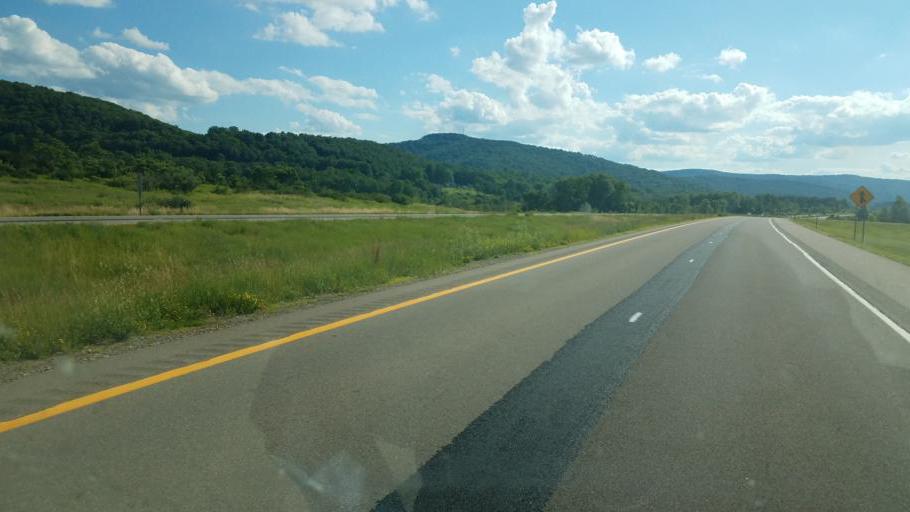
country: US
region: New York
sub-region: Cattaraugus County
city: Allegany
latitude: 42.0949
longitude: -78.5367
